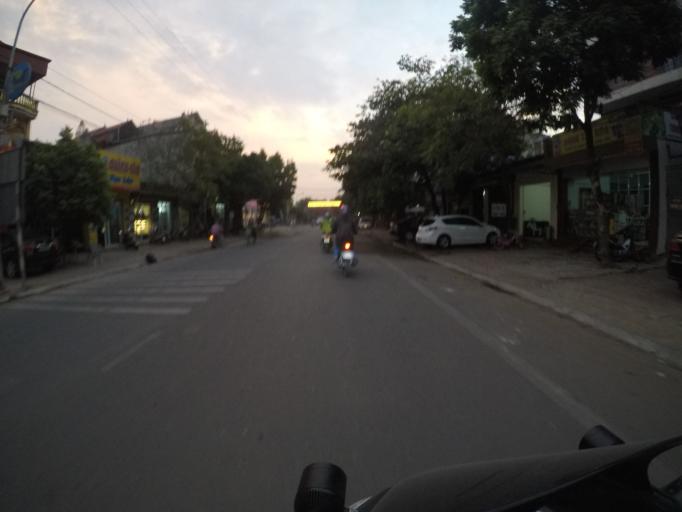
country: VN
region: Vinh Phuc
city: Phuc Yen
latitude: 21.2773
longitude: 105.7291
